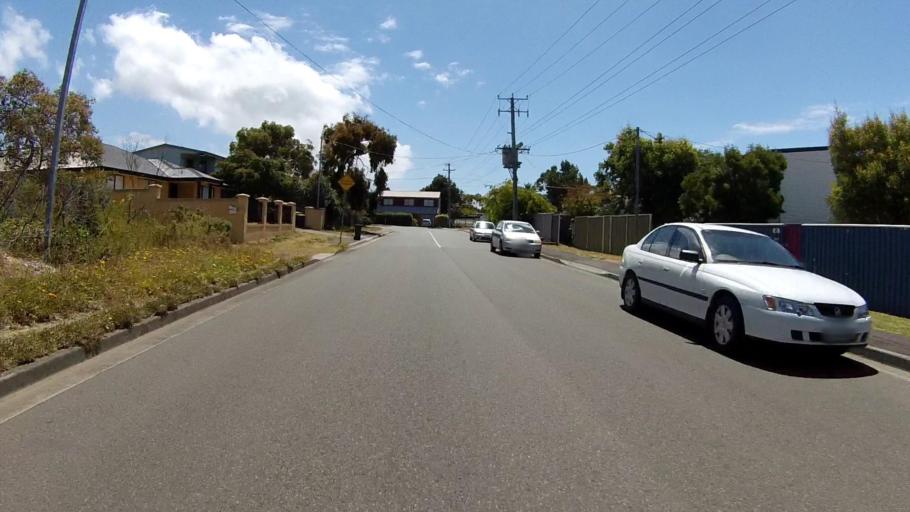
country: AU
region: Tasmania
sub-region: Clarence
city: Lauderdale
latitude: -42.9138
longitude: 147.4963
